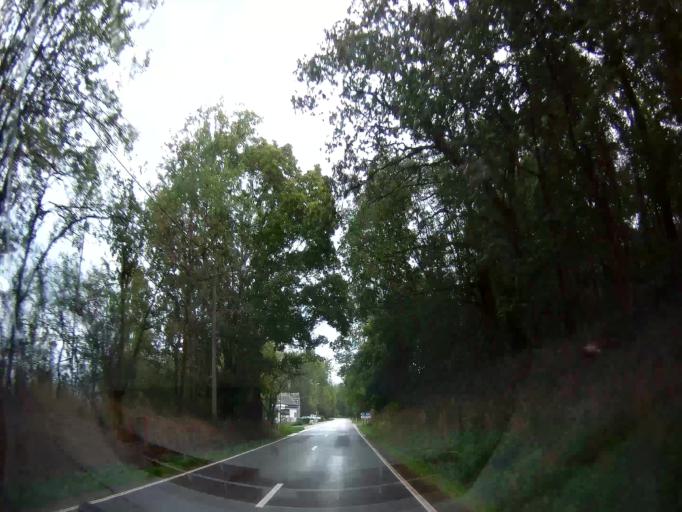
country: BE
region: Wallonia
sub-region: Province de Liege
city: Ferrieres
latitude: 50.4253
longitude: 5.6008
